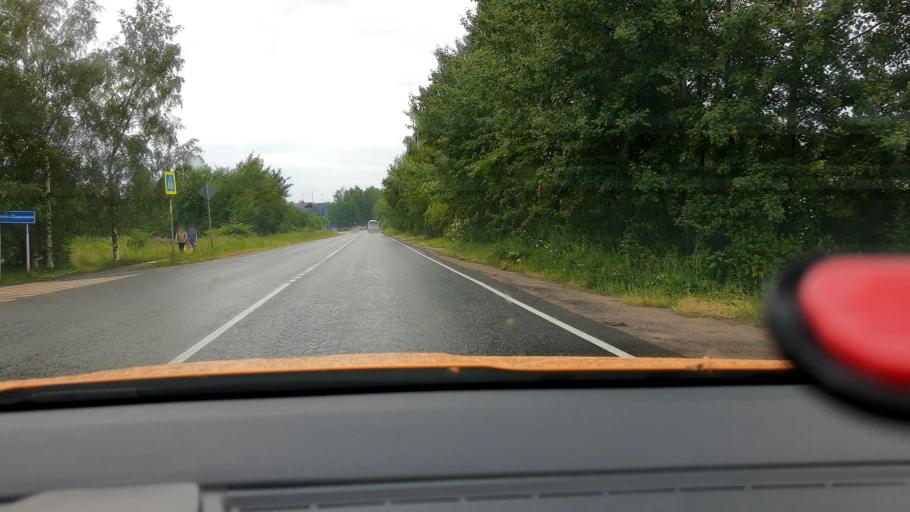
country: RU
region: Moskovskaya
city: Povedniki
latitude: 55.9932
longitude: 37.6655
